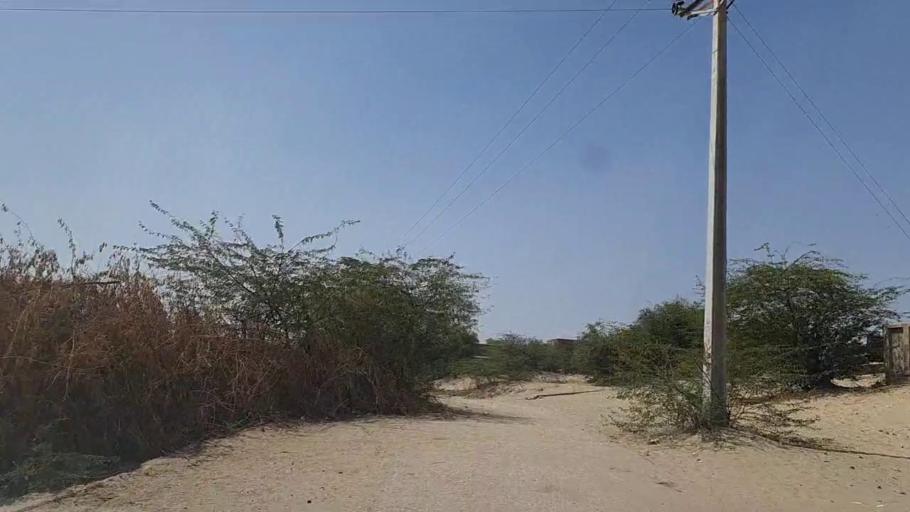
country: PK
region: Sindh
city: Diplo
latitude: 24.4838
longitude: 69.4625
